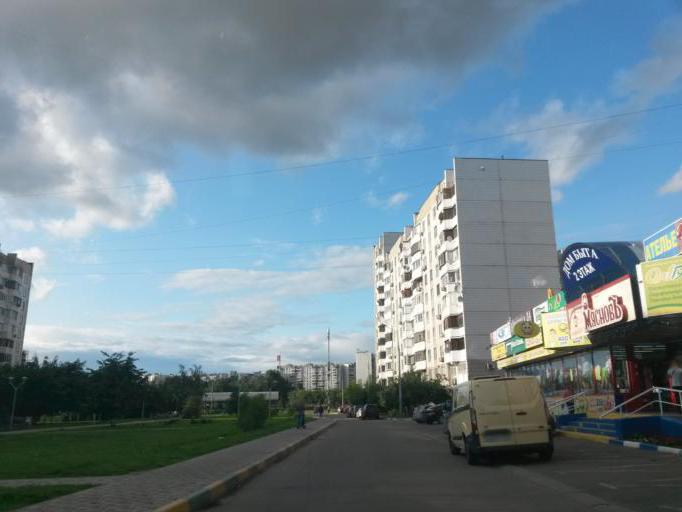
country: RU
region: Moscow
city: Zhulebino
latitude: 55.6906
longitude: 37.8543
